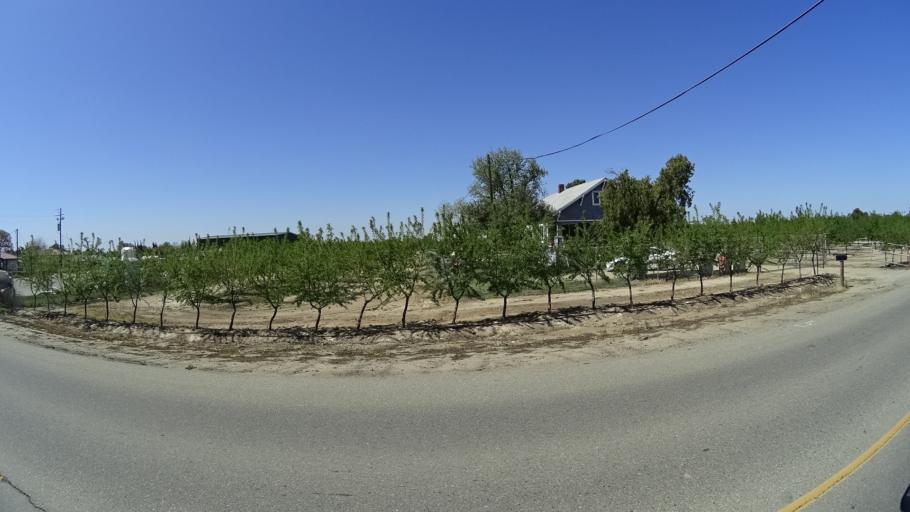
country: US
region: California
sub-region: Fresno County
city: West Park
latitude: 36.7164
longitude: -119.8445
